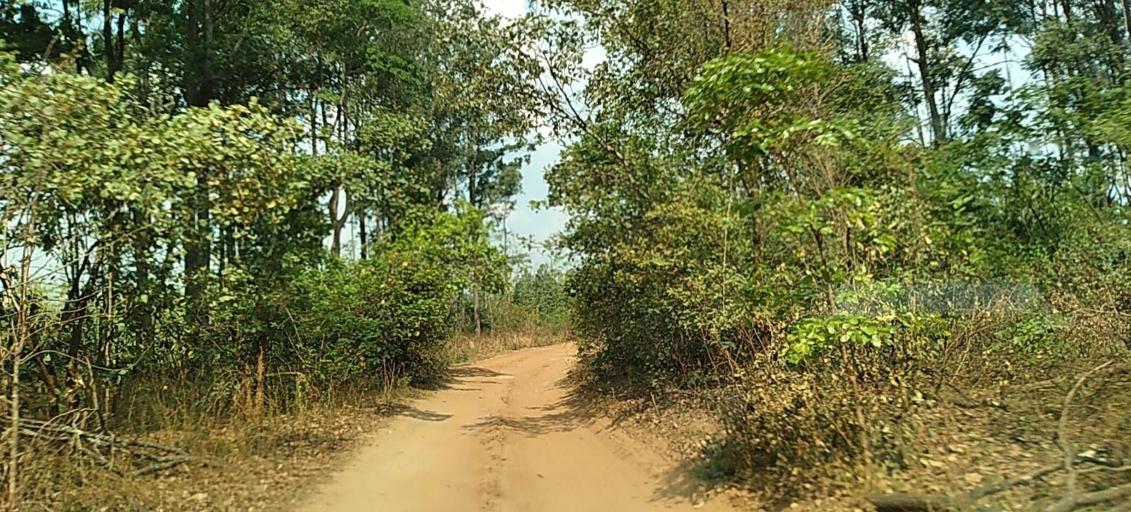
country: ZM
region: Copperbelt
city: Chingola
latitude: -12.7382
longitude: 27.7686
